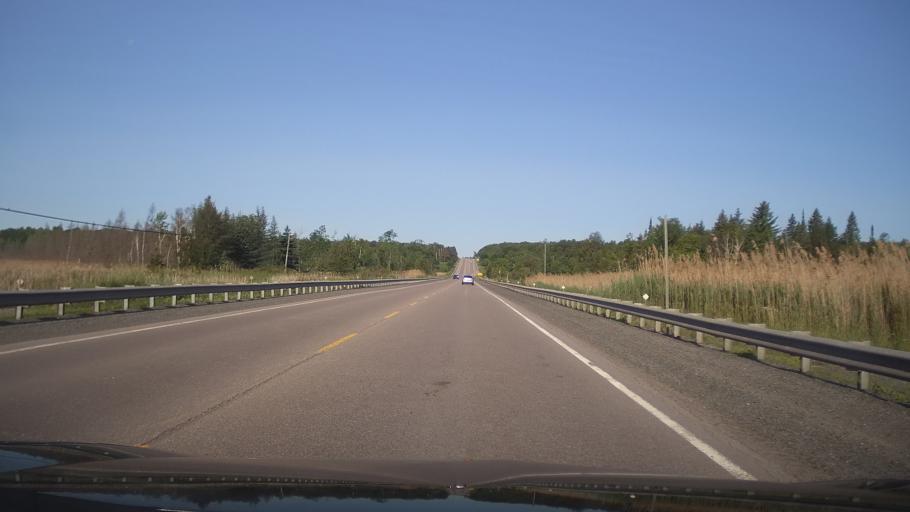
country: CA
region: Ontario
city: Quinte West
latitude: 44.4932
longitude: -77.6433
